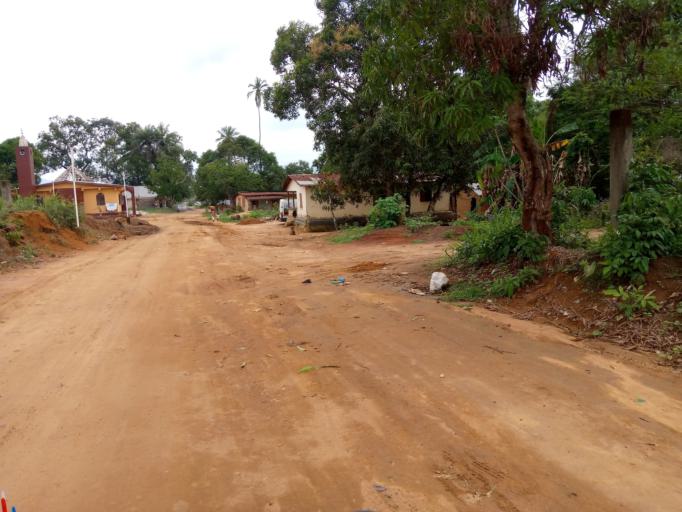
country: SL
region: Western Area
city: Waterloo
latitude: 8.3377
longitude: -13.0173
